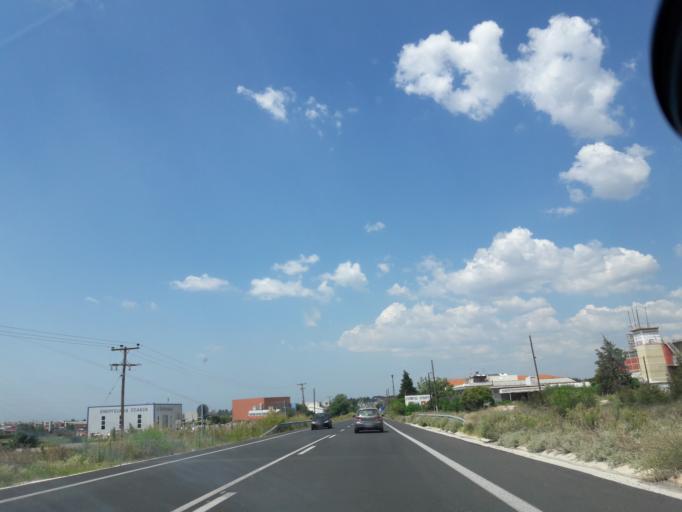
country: GR
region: Central Macedonia
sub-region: Nomos Thessalonikis
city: Agia Paraskevi
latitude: 40.5147
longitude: 23.0725
